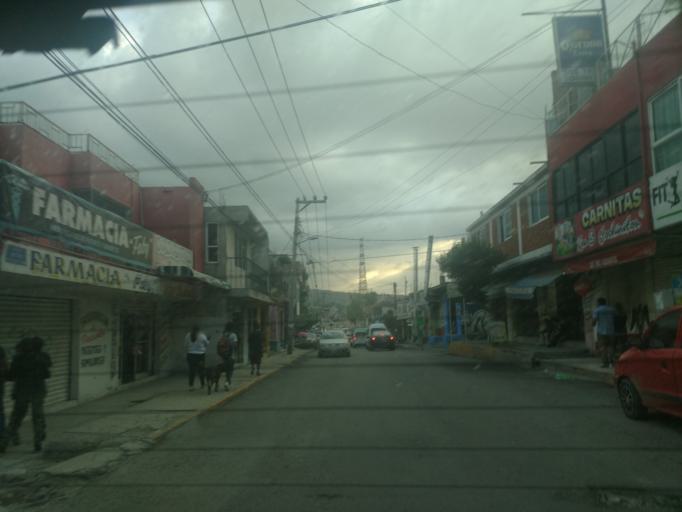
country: MX
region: Morelos
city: Coyotepec
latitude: 19.7774
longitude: -99.2166
